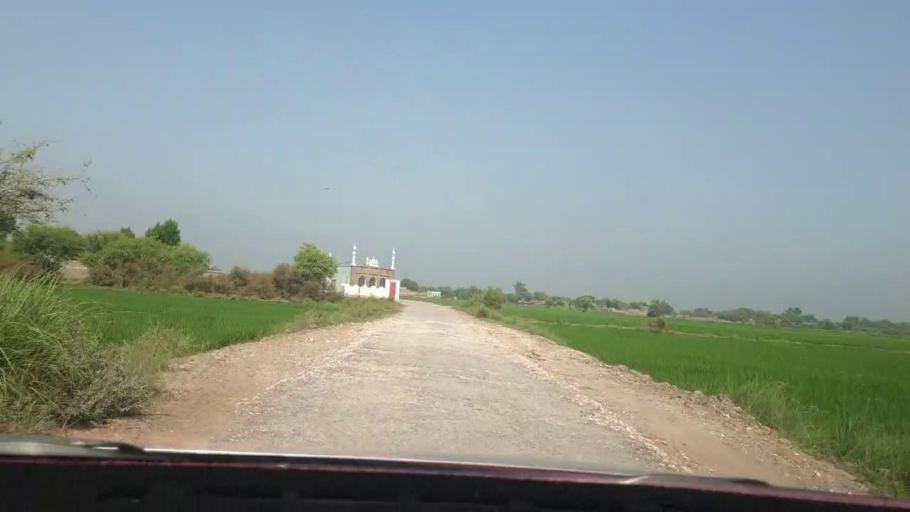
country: PK
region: Sindh
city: Nasirabad
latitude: 27.4321
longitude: 67.8936
